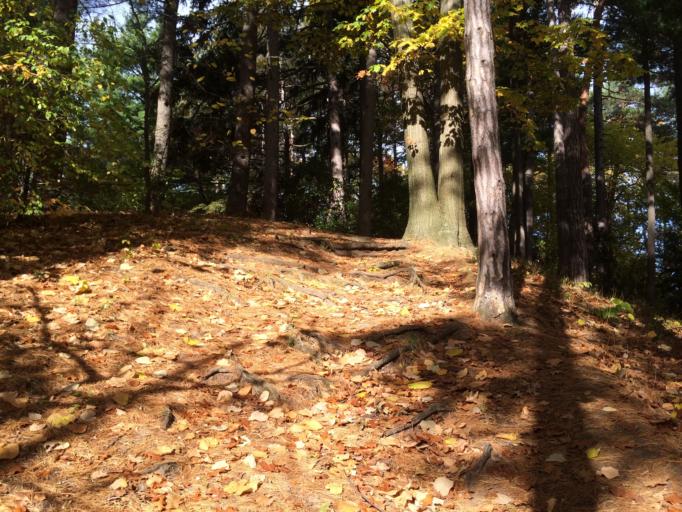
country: US
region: New York
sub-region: Monroe County
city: Rochester
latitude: 43.1324
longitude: -77.6005
